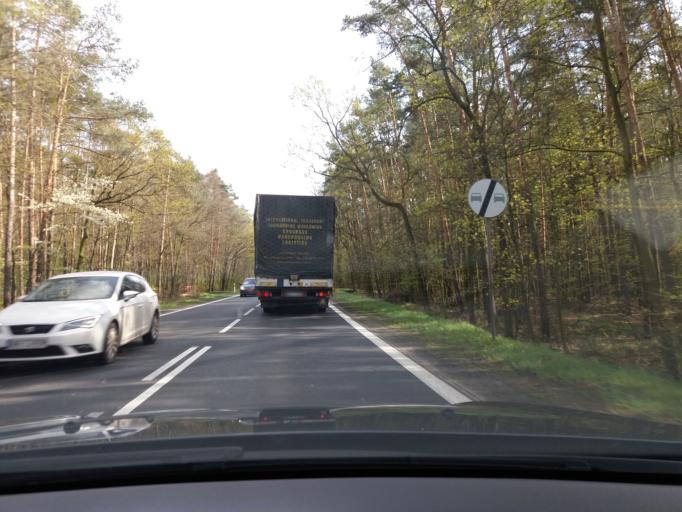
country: PL
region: Lower Silesian Voivodeship
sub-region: Powiat sredzki
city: Malczyce
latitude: 51.1787
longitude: 16.5299
